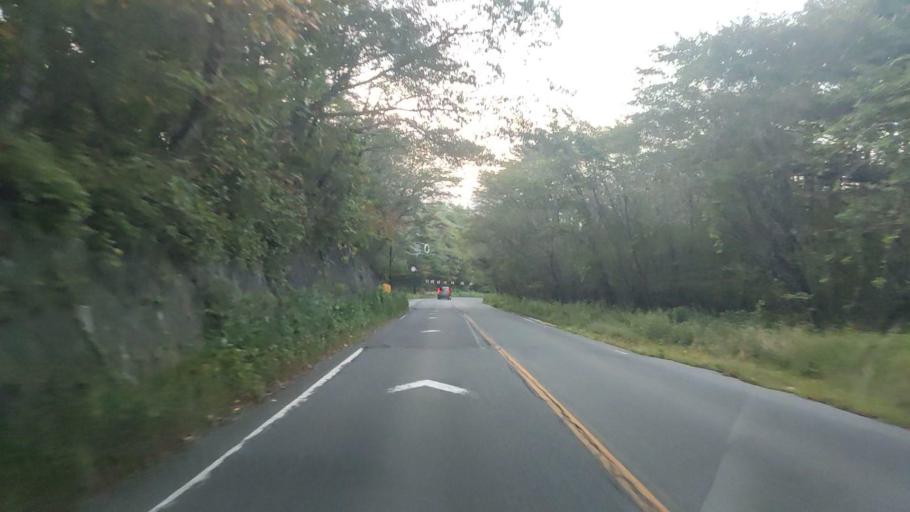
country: JP
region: Nagano
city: Komoro
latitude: 36.4269
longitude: 138.5714
